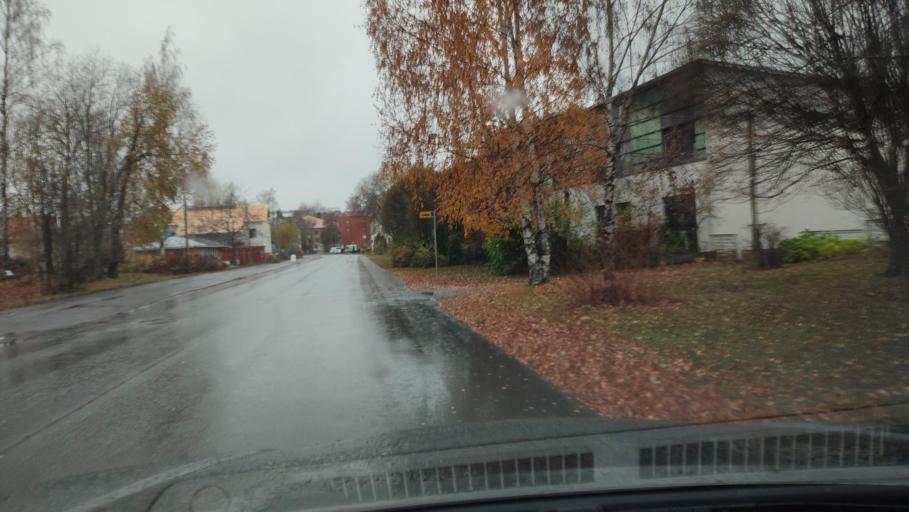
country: FI
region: Ostrobothnia
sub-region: Vaasa
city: Vaasa
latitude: 63.0907
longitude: 21.6345
